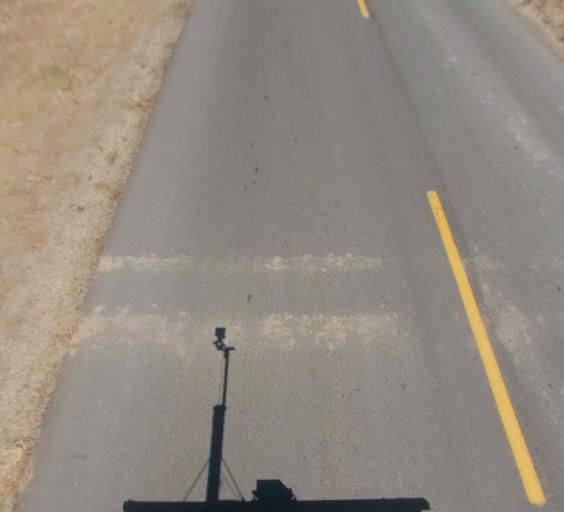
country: US
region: California
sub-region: Madera County
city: Madera Acres
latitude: 37.0491
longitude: -120.0019
